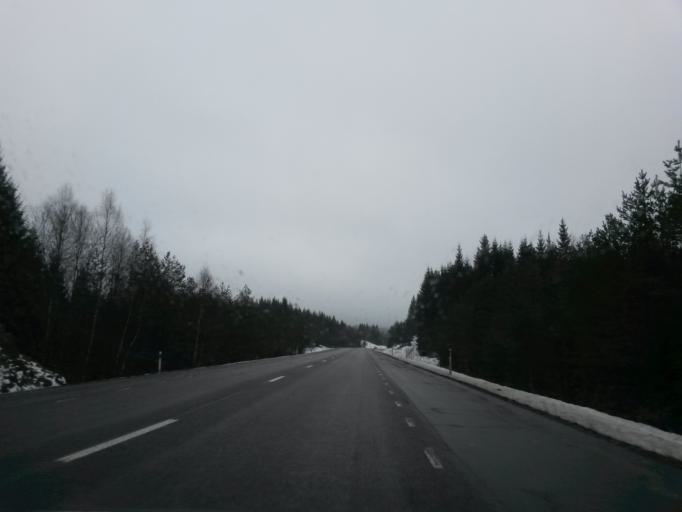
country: SE
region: Vaestra Goetaland
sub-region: Boras Kommun
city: Viskafors
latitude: 57.6069
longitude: 12.8728
